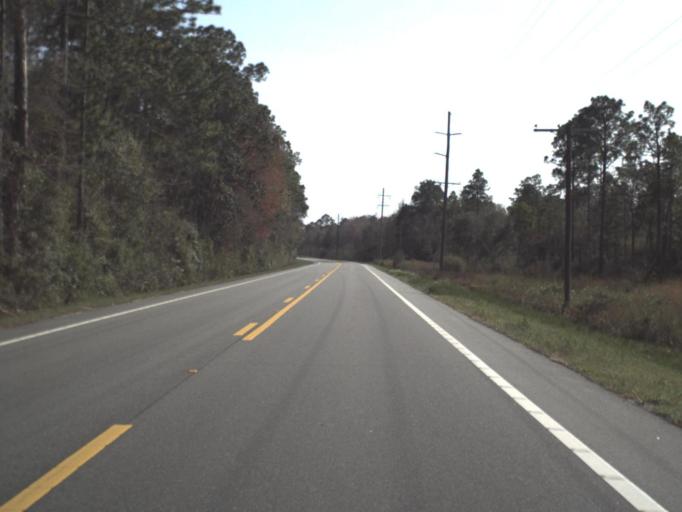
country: US
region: Florida
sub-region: Franklin County
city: Carrabelle
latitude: 29.9992
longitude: -84.5041
